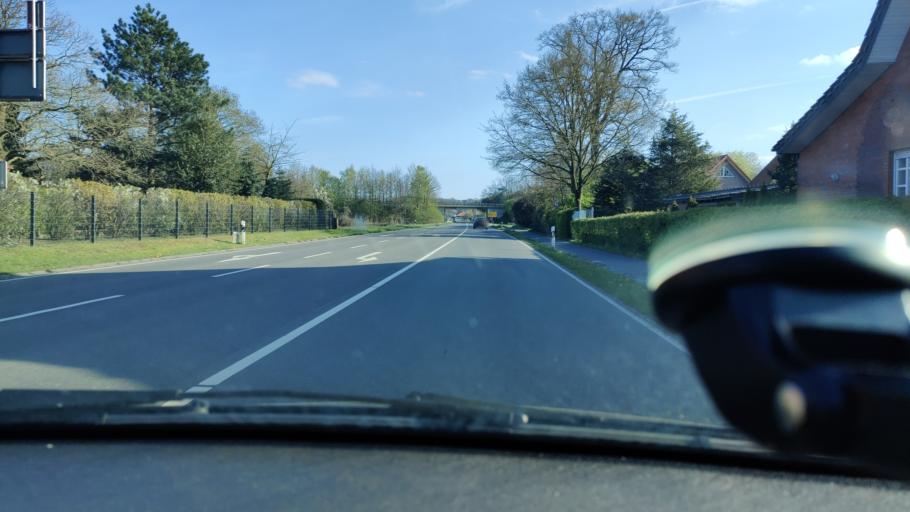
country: DE
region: North Rhine-Westphalia
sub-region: Regierungsbezirk Munster
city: Klein Reken
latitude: 51.8544
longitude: 7.0537
